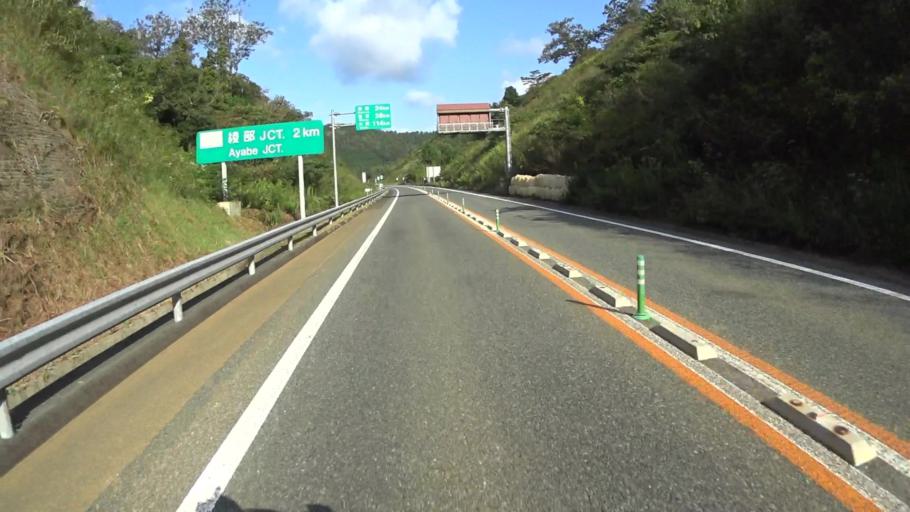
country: JP
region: Kyoto
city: Ayabe
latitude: 35.3400
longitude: 135.3053
